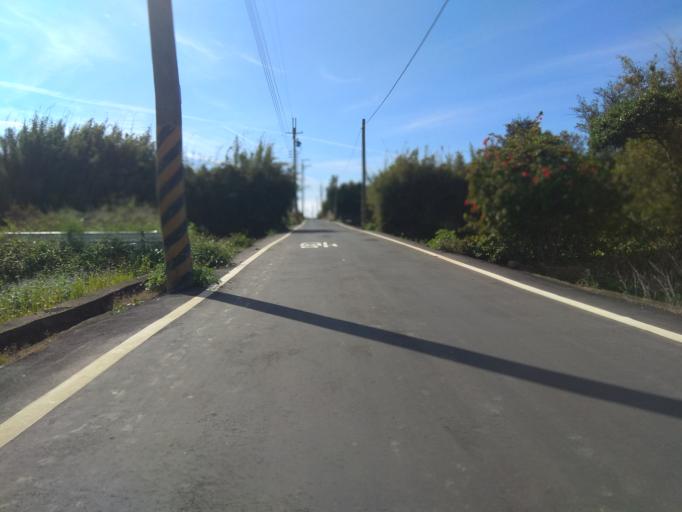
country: TW
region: Taiwan
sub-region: Hsinchu
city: Zhubei
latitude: 24.9935
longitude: 121.0411
